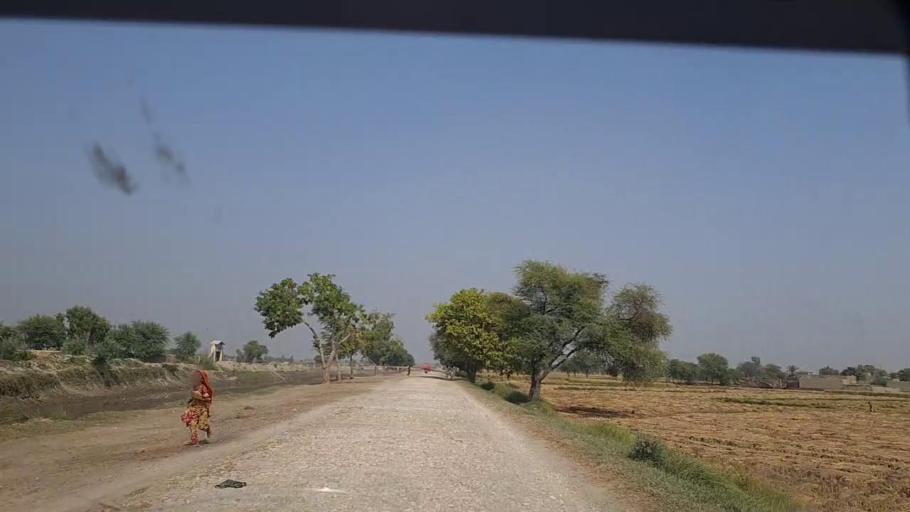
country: PK
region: Sindh
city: Thul
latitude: 28.1106
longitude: 68.6949
